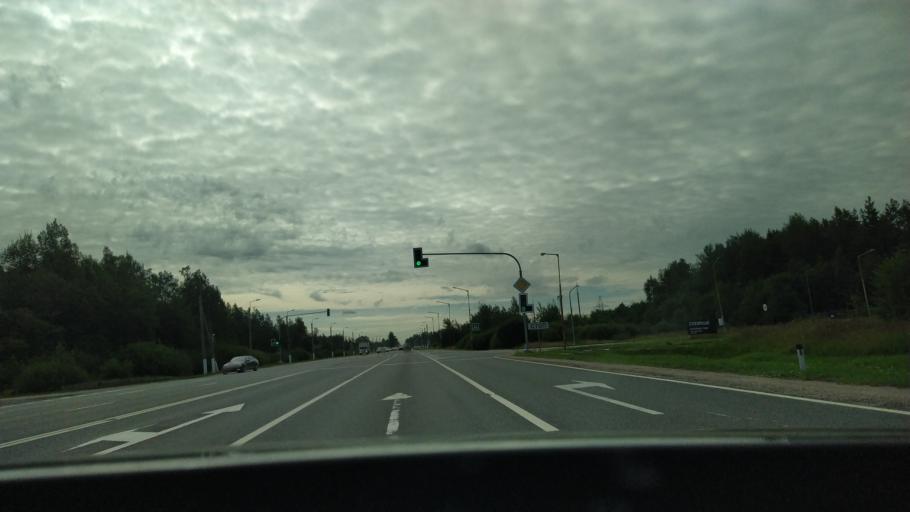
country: RU
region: Leningrad
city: Tosno
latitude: 59.5689
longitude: 30.8261
